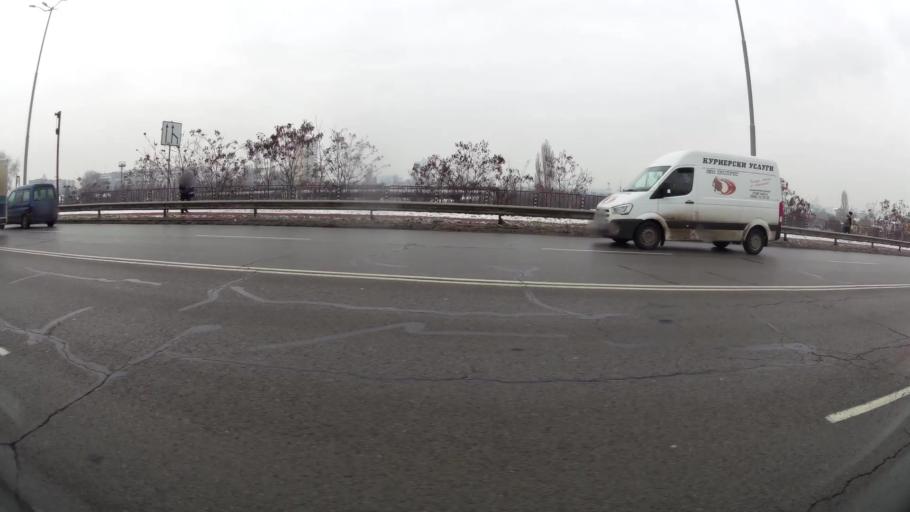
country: BG
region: Sofia-Capital
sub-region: Stolichna Obshtina
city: Sofia
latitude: 42.7176
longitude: 23.3100
